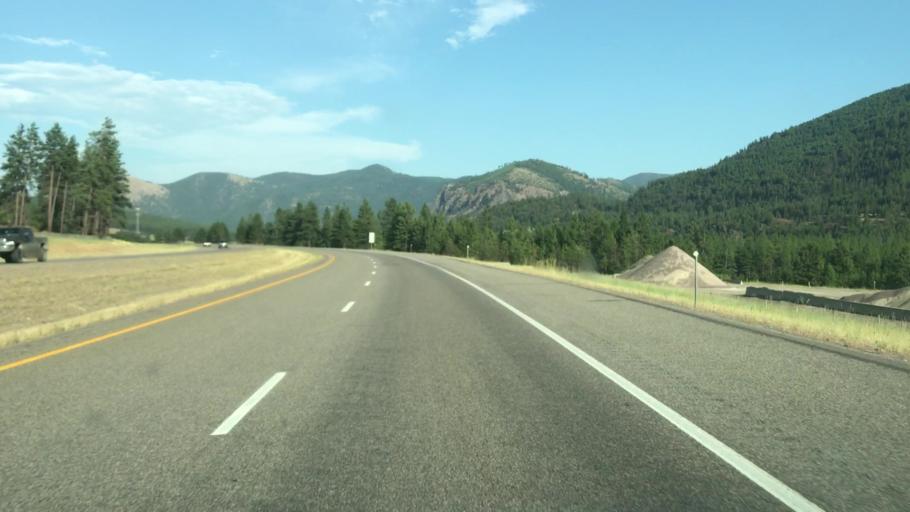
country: US
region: Montana
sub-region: Missoula County
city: Frenchtown
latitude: 47.0014
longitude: -114.4855
